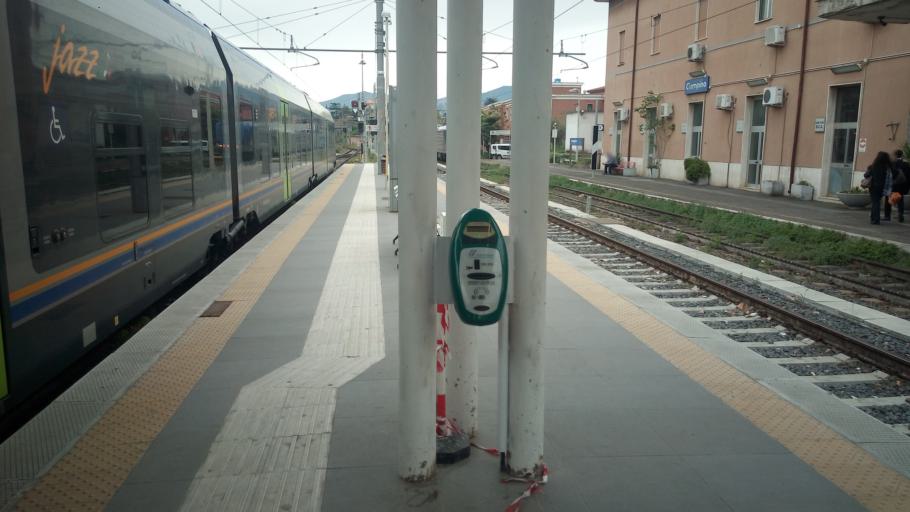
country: IT
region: Latium
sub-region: Citta metropolitana di Roma Capitale
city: Ciampino
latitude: 41.8041
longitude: 12.5997
